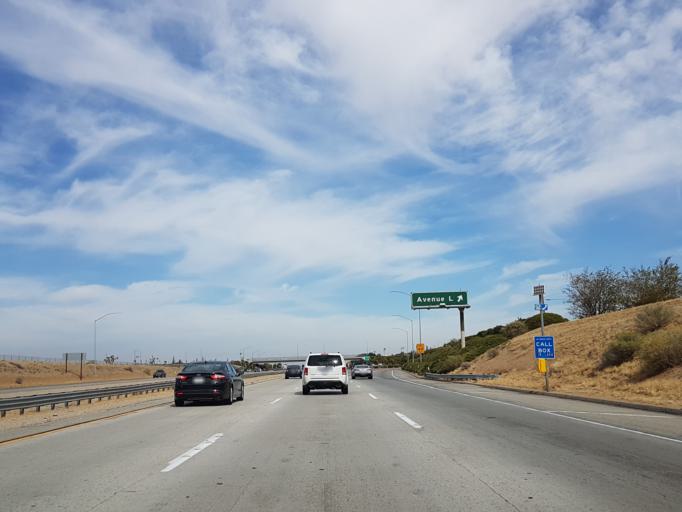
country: US
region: California
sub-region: Los Angeles County
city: Lancaster
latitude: 34.6556
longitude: -118.1532
